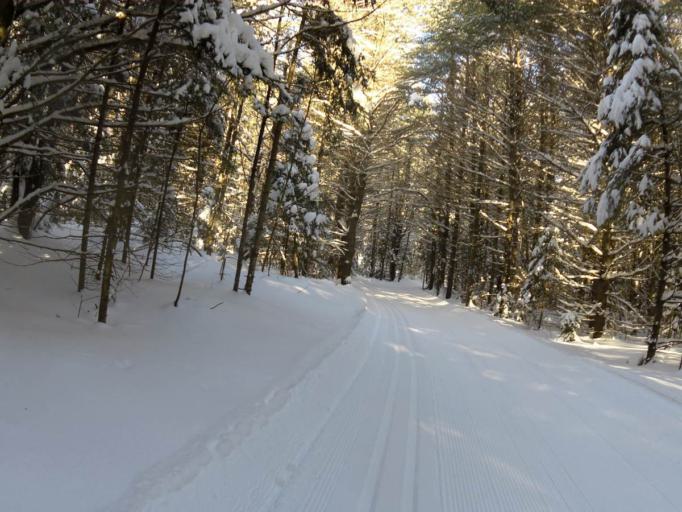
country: CA
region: Quebec
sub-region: Outaouais
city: Wakefield
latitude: 45.6256
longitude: -75.9484
